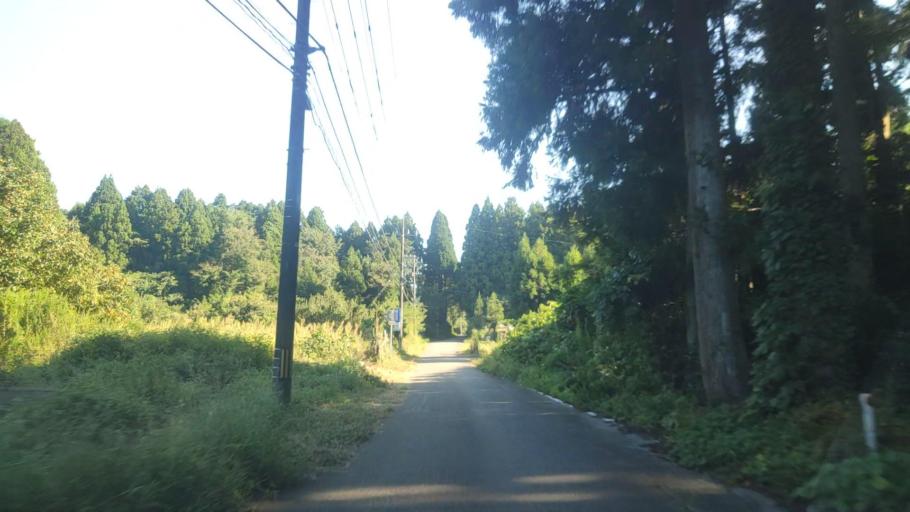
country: JP
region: Ishikawa
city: Nanao
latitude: 37.1361
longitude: 136.9090
